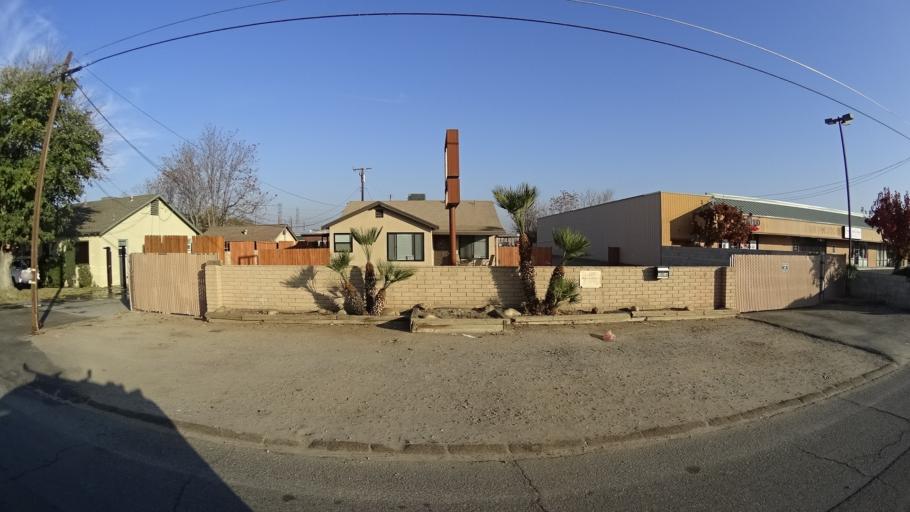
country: US
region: California
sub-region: Kern County
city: Greenacres
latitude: 35.3836
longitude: -119.1133
